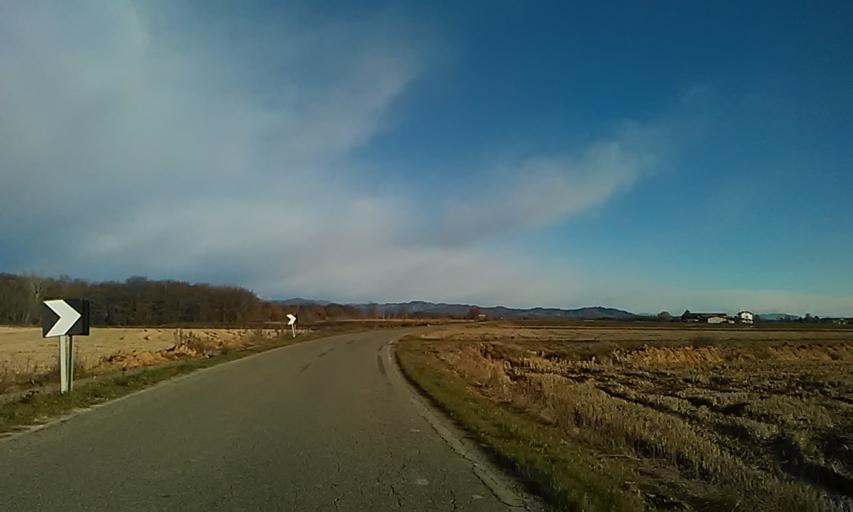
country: IT
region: Piedmont
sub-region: Provincia di Vercelli
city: Rovasenda
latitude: 45.5403
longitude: 8.2738
